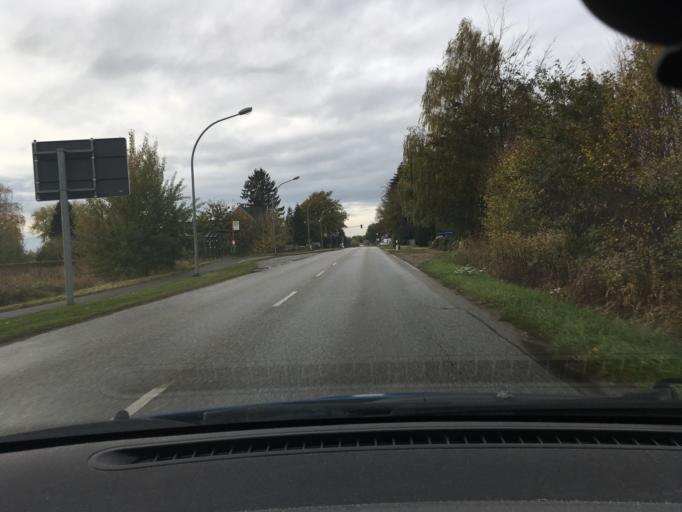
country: DE
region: Schleswig-Holstein
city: Bornsen
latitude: 53.4876
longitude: 10.2863
